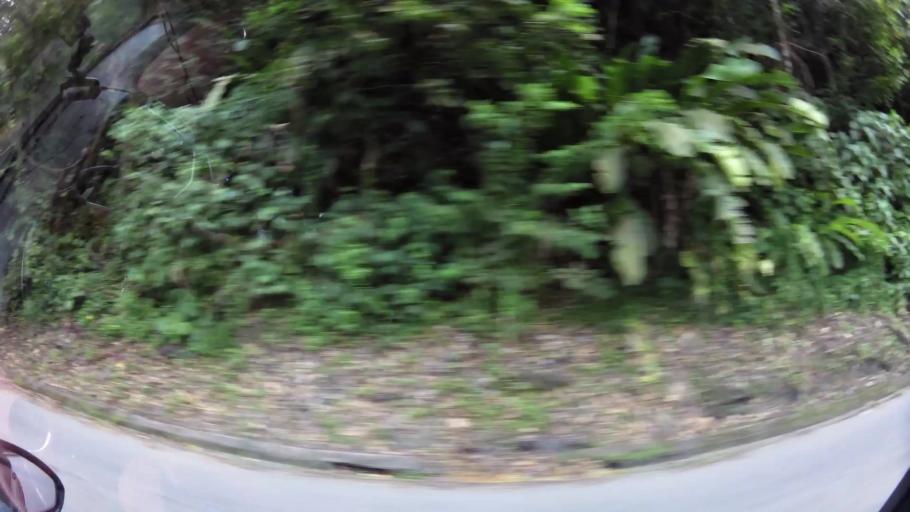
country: TT
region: Diego Martin
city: Petit Valley
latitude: 10.7479
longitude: -61.4814
